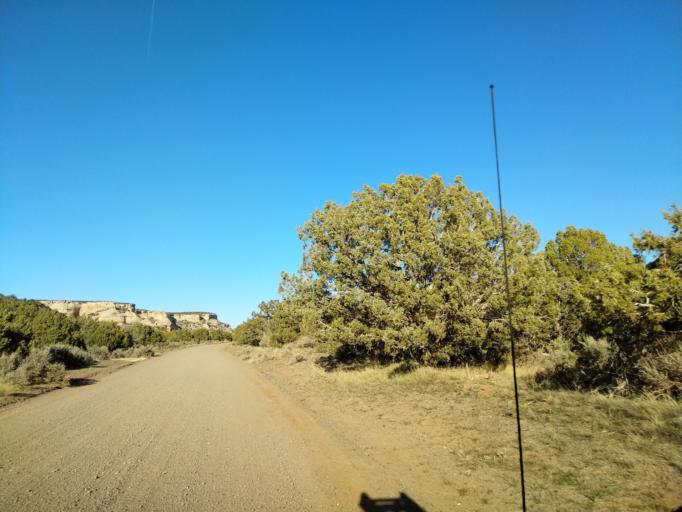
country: US
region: Colorado
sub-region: Mesa County
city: Loma
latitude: 38.9508
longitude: -109.0596
